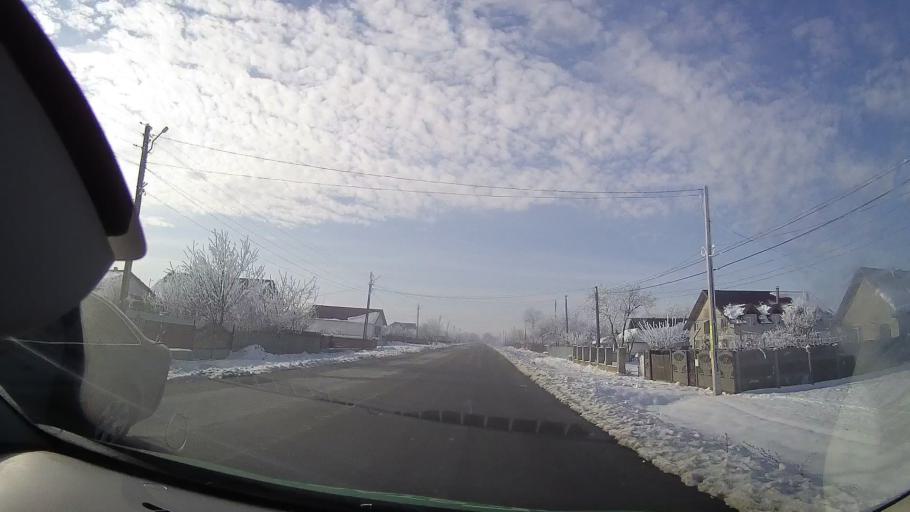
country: RO
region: Neamt
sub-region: Comuna Timisesti
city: Timisesti
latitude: 47.2329
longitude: 26.5238
